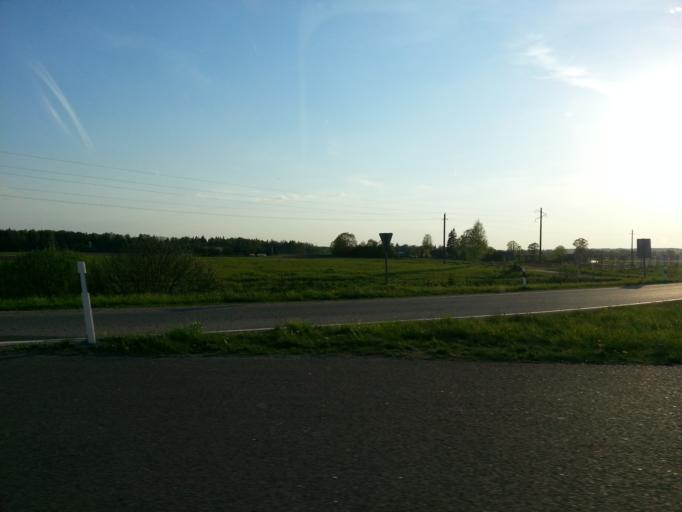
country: LT
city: Sirvintos
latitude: 55.0655
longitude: 24.8854
